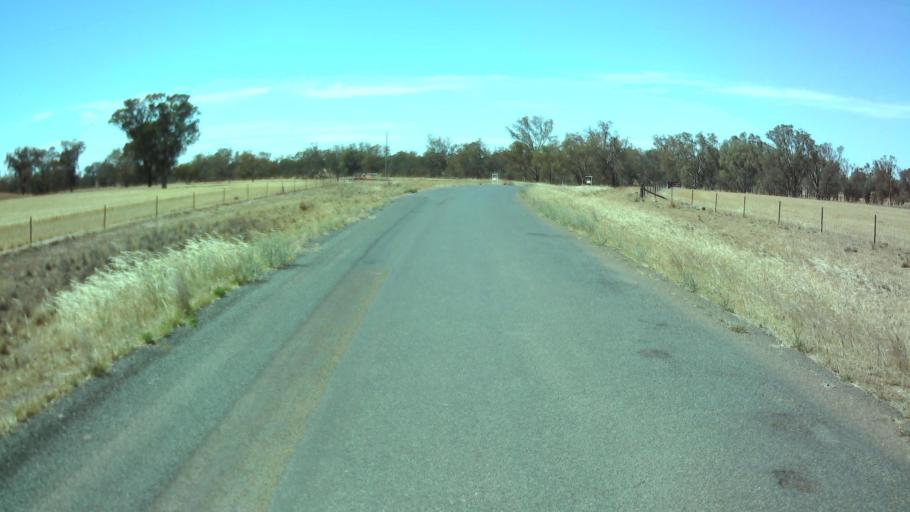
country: AU
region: New South Wales
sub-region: Weddin
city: Grenfell
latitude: -34.0999
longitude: 147.8864
